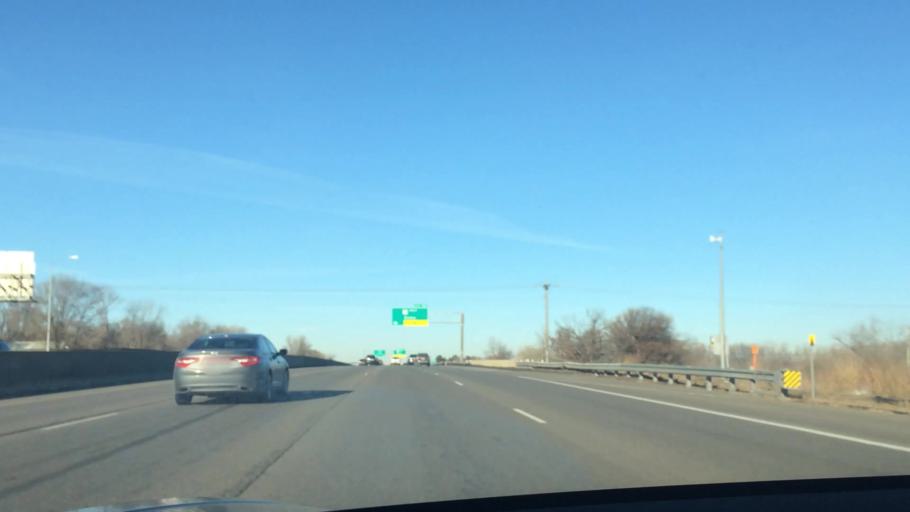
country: US
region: Minnesota
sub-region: Ramsey County
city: Mounds View
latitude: 45.1071
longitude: -93.1882
